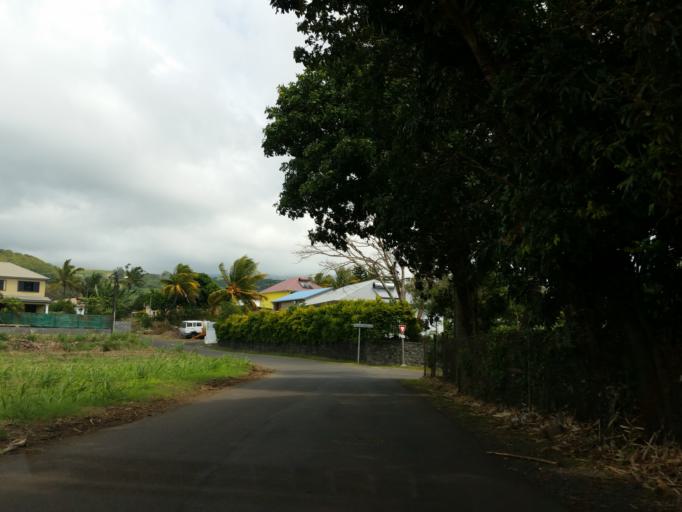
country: RE
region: Reunion
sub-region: Reunion
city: Sainte-Suzanne
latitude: -20.9168
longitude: 55.6136
